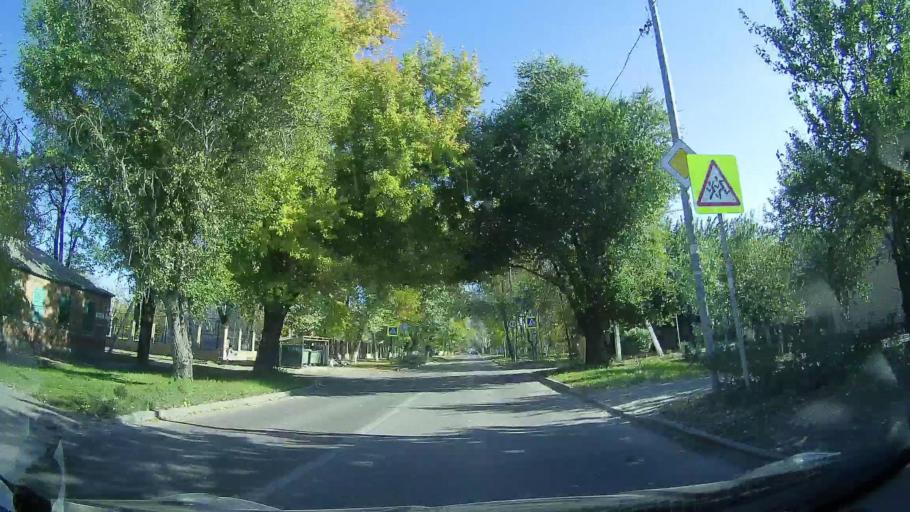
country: RU
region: Rostov
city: Rostov-na-Donu
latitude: 47.2409
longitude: 39.6758
